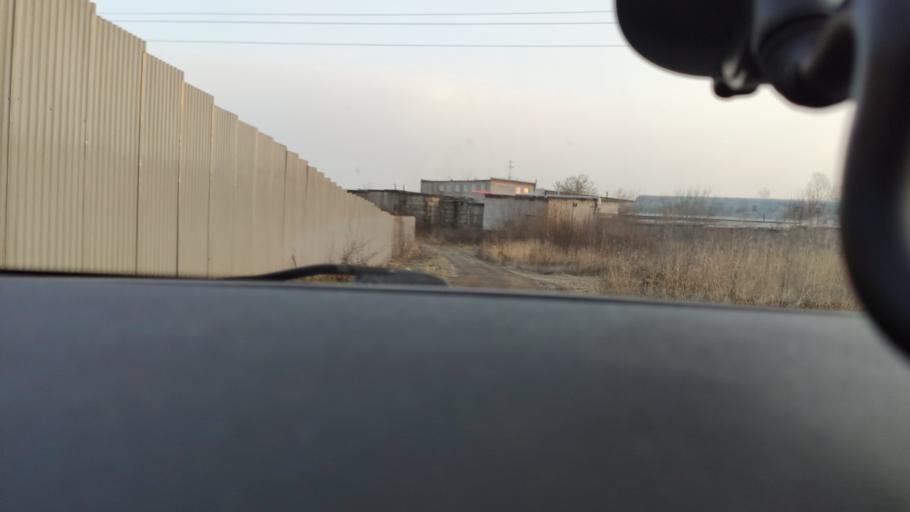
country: RU
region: Perm
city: Kondratovo
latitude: 57.9974
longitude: 56.1143
